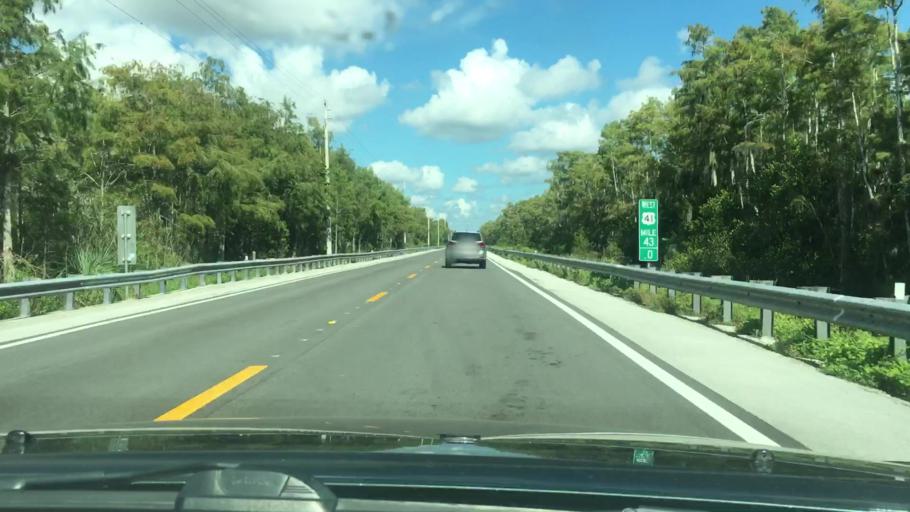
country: US
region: Florida
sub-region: Miami-Dade County
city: Kendall West
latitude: 25.7971
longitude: -80.8645
